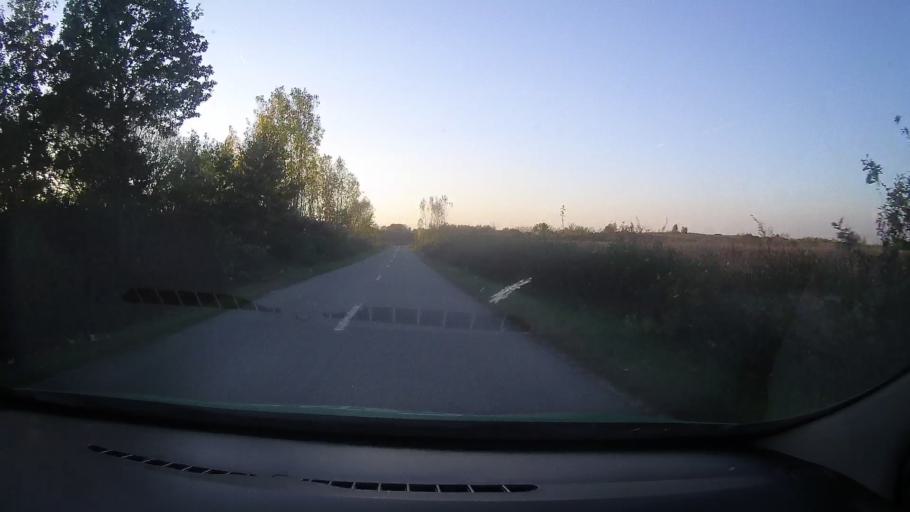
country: RO
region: Timis
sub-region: Comuna Traian Vuia
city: Traian Vuia
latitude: 45.7867
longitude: 22.0387
